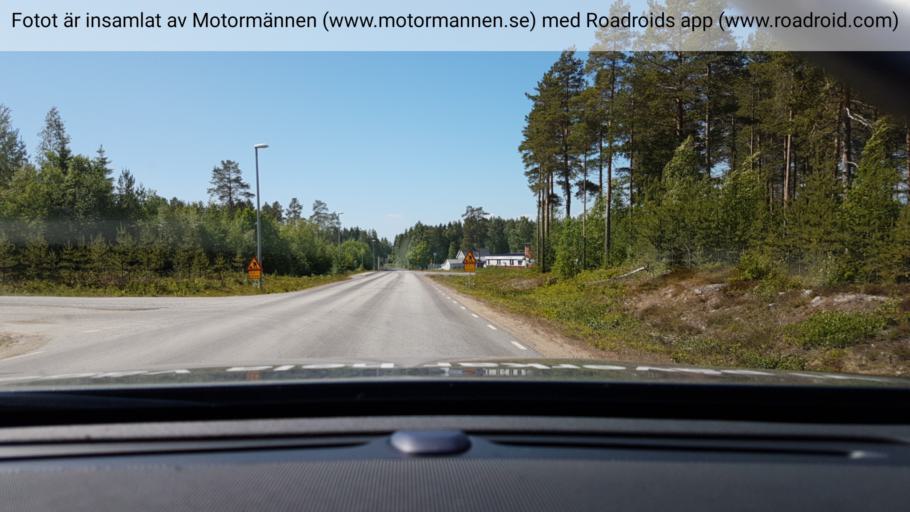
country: SE
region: Vaesterbotten
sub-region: Nordmalings Kommun
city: Nordmaling
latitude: 63.5799
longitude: 19.5323
